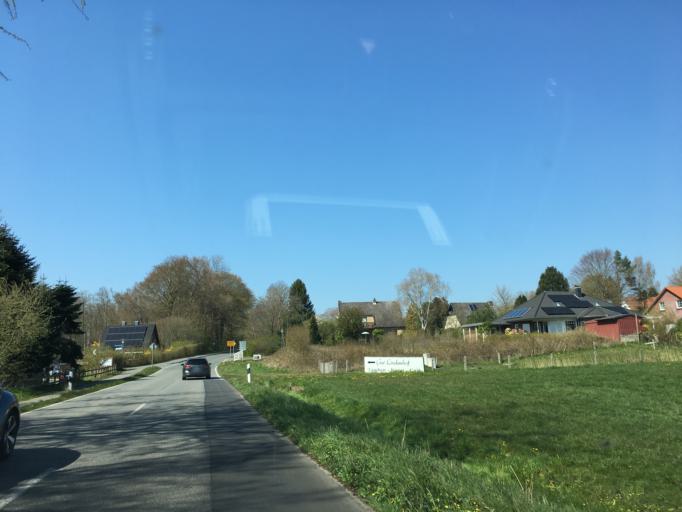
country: DE
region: Schleswig-Holstein
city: Dollrottfeld
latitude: 54.5898
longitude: 9.8059
